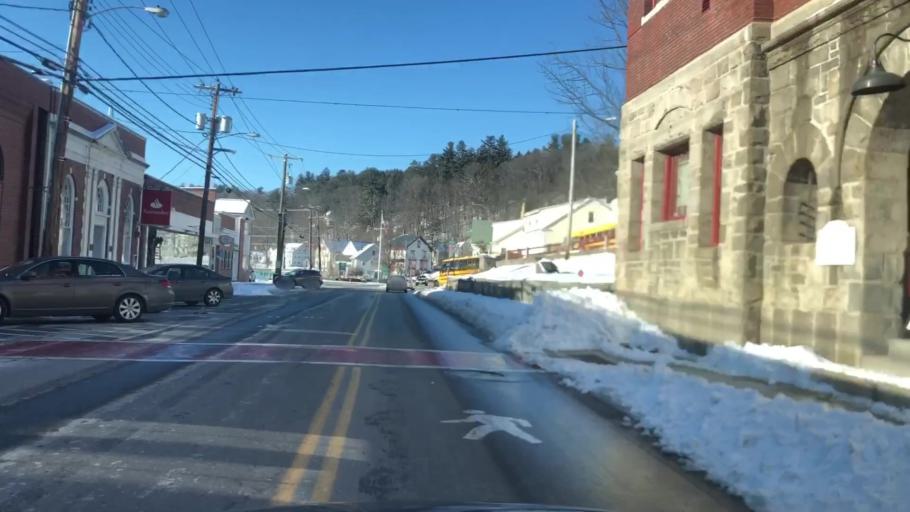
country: US
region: New Hampshire
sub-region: Hillsborough County
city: Wilton
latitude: 42.8437
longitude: -71.7378
